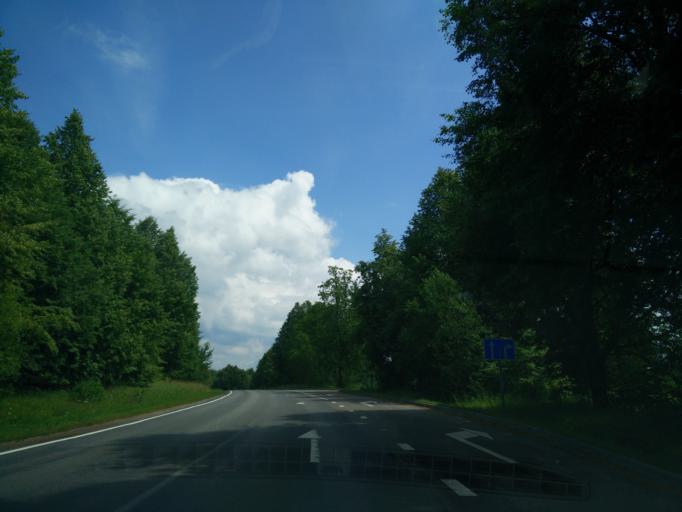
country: LT
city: Skaidiskes
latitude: 54.6917
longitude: 25.4647
